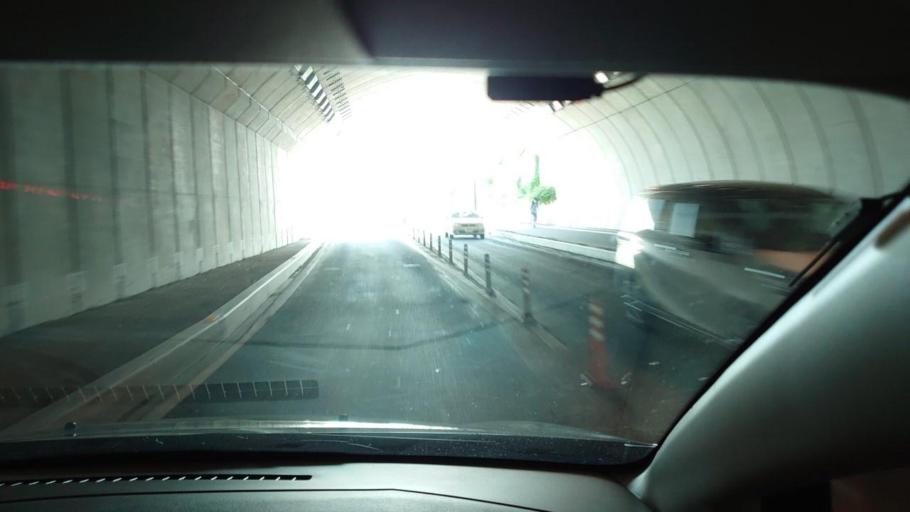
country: JP
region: Iwate
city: Morioka-shi
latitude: 39.6932
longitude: 141.1272
